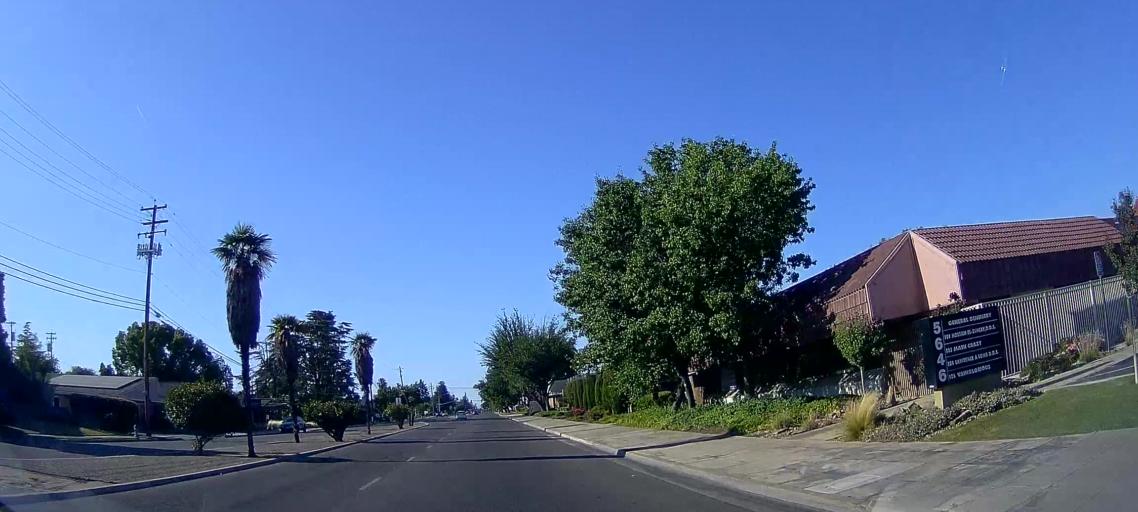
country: US
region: California
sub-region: Fresno County
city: Fresno
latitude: 36.8197
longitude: -119.8083
